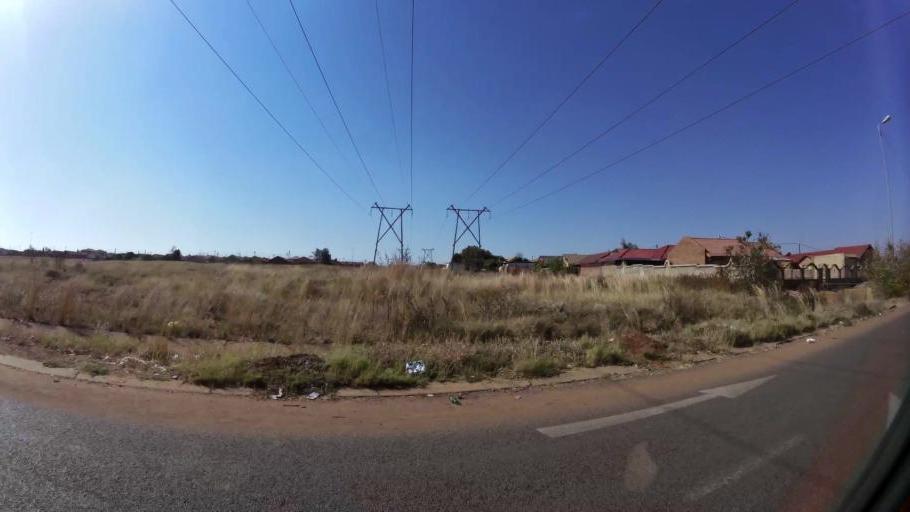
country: ZA
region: Gauteng
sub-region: City of Tshwane Metropolitan Municipality
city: Mabopane
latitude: -25.5590
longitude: 28.0759
